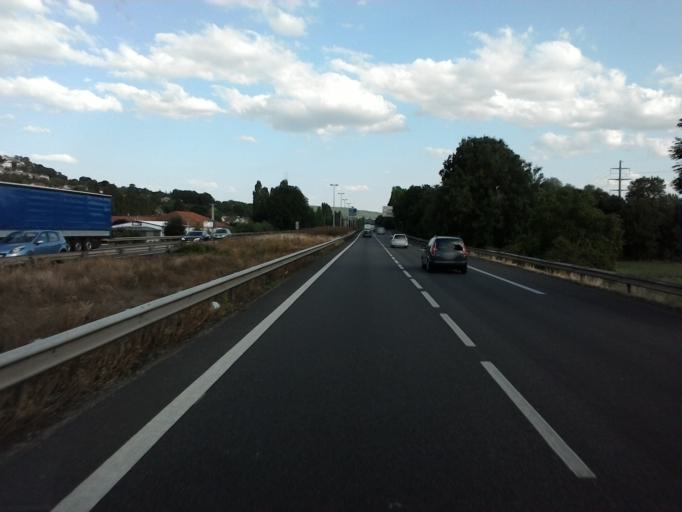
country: FR
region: Lorraine
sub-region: Departement de Meurthe-et-Moselle
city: Frouard
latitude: 48.7587
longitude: 6.1508
